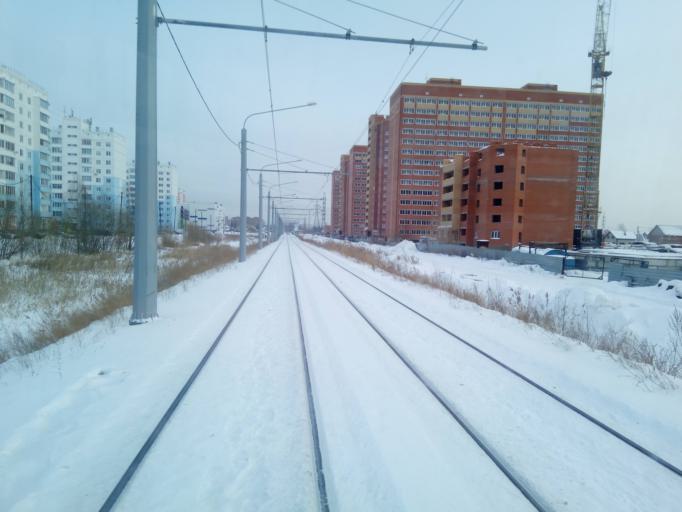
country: RU
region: Novosibirsk
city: Tolmachevo
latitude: 54.9787
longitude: 82.8056
